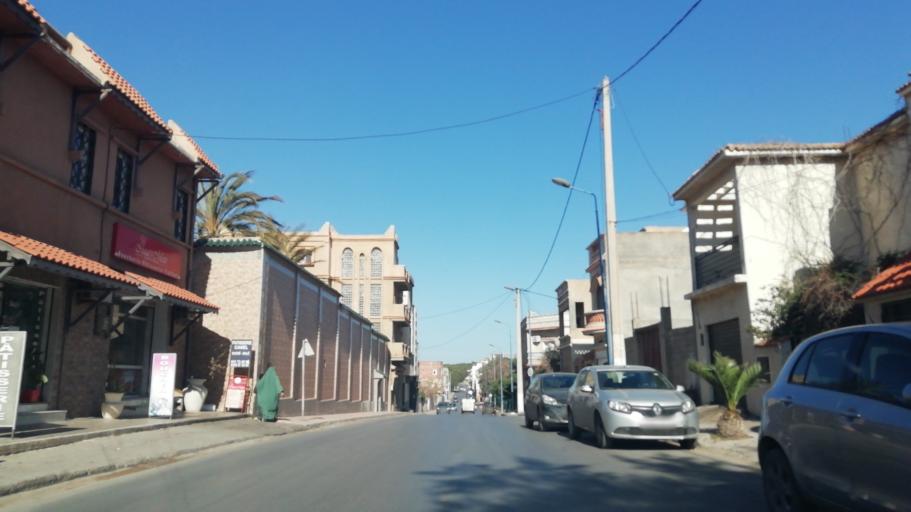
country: DZ
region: Oran
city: Bir el Djir
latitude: 35.7493
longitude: -0.5671
